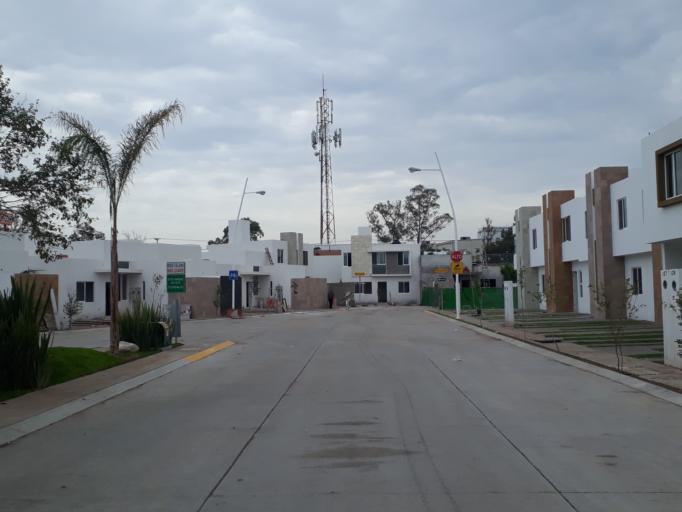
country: MX
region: Aguascalientes
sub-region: Aguascalientes
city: La Loma de los Negritos
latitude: 21.8423
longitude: -102.3255
